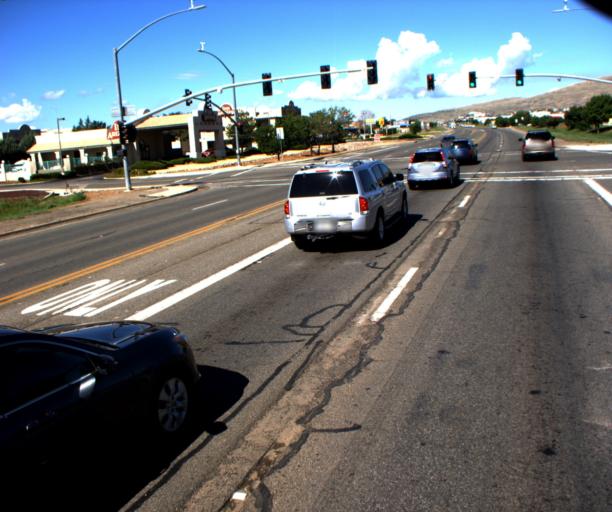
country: US
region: Arizona
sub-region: Yavapai County
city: Prescott Valley
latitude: 34.5860
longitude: -112.3264
